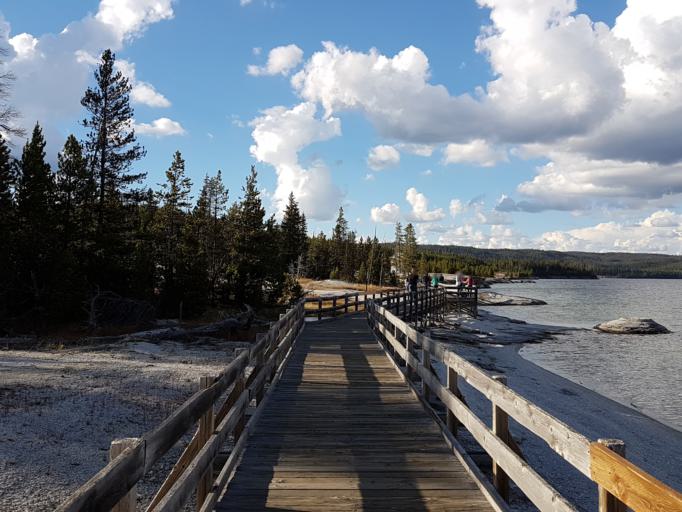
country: US
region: Montana
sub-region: Gallatin County
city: West Yellowstone
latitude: 44.4168
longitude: -110.5701
